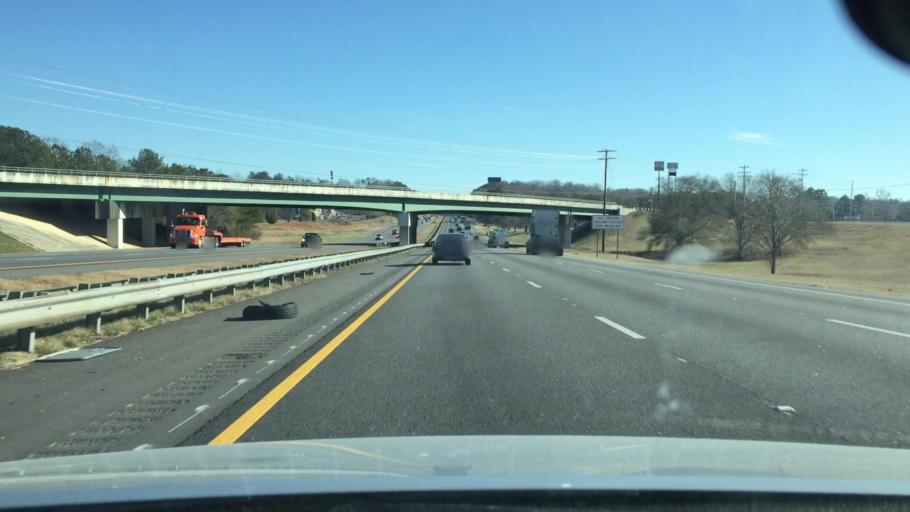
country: US
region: Georgia
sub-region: Catoosa County
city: Ringgold
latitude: 34.8931
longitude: -85.0761
